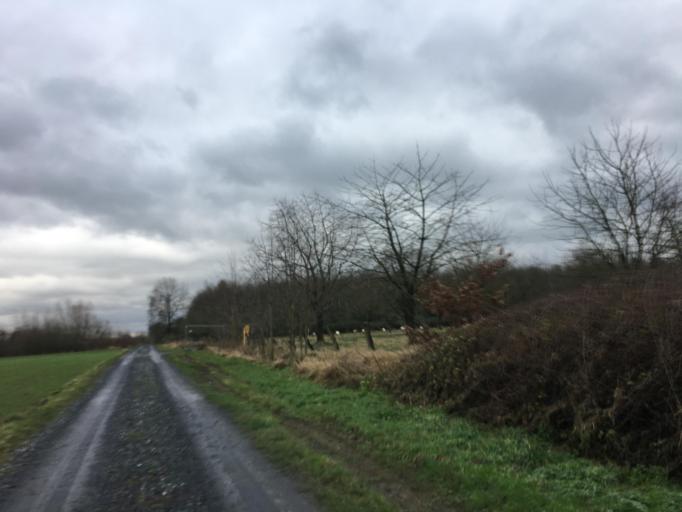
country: DE
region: North Rhine-Westphalia
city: Ludinghausen
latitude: 51.7708
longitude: 7.3891
